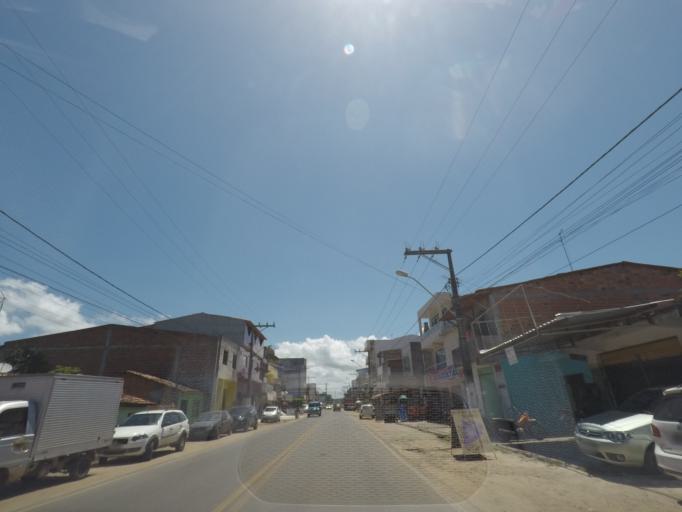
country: BR
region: Bahia
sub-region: Valenca
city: Valenca
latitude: -13.3563
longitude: -39.0632
